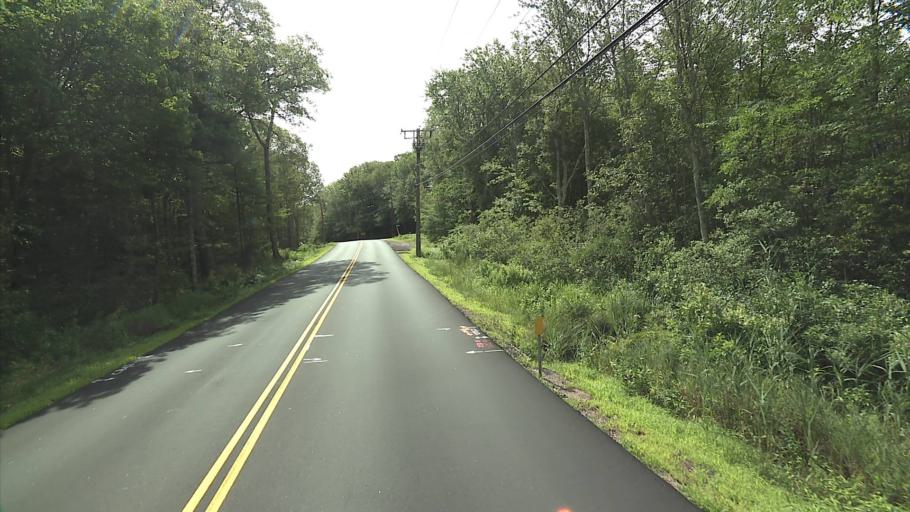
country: US
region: Connecticut
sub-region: Windham County
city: South Woodstock
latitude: 41.9410
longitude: -72.0031
